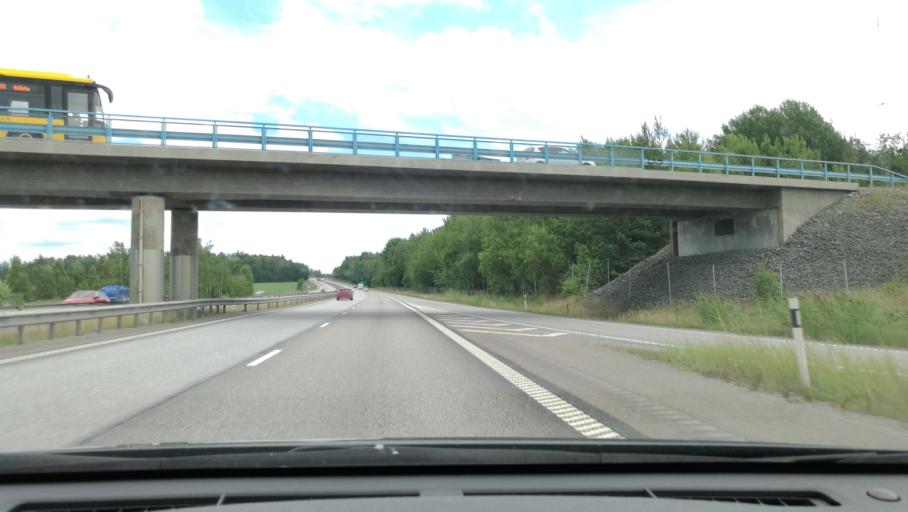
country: SE
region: Uppsala
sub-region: Habo Kommun
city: Balsta
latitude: 59.5863
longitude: 17.5072
